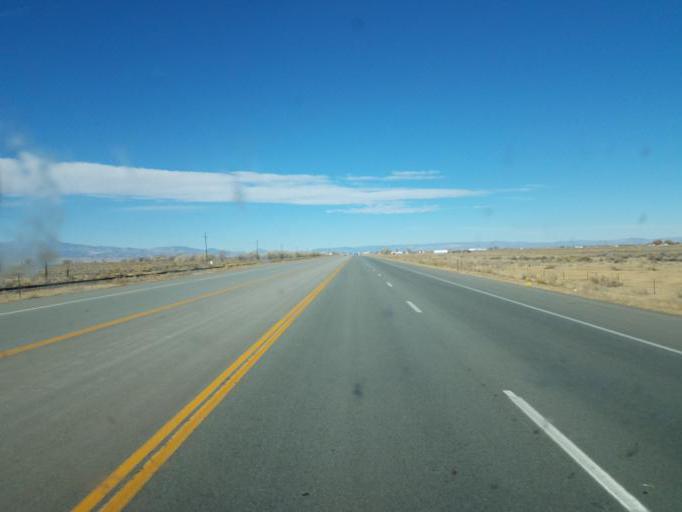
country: US
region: Colorado
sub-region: Alamosa County
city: Alamosa
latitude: 37.5159
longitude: -105.9904
